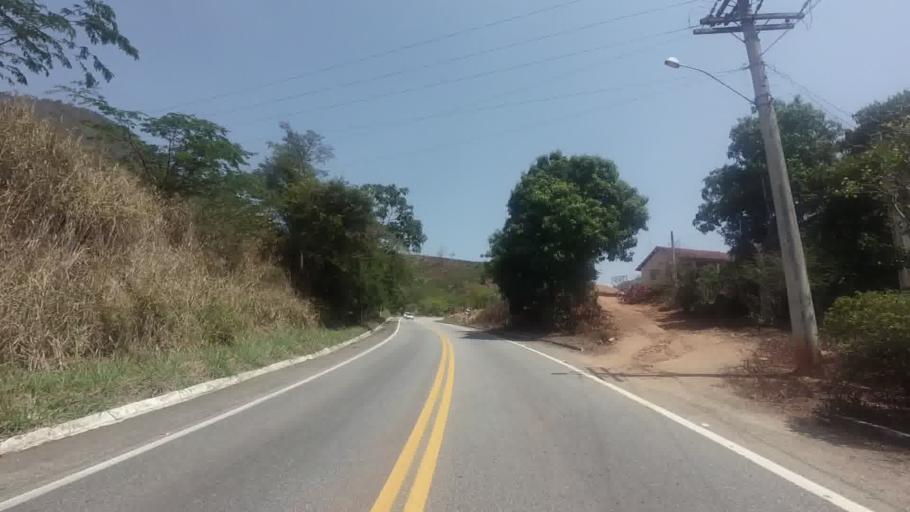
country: BR
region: Espirito Santo
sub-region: Cachoeiro De Itapemirim
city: Cachoeiro de Itapemirim
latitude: -20.8383
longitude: -41.2309
